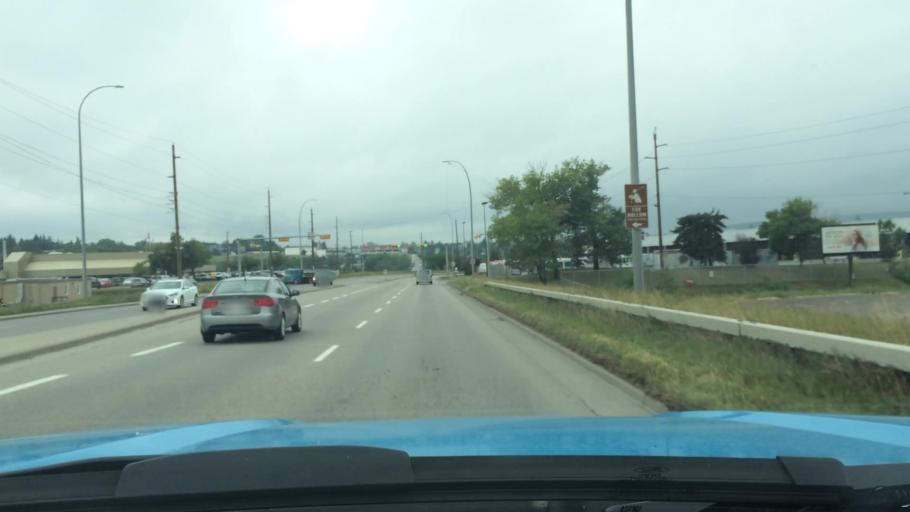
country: CA
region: Alberta
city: Calgary
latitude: 51.0816
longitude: -114.0398
